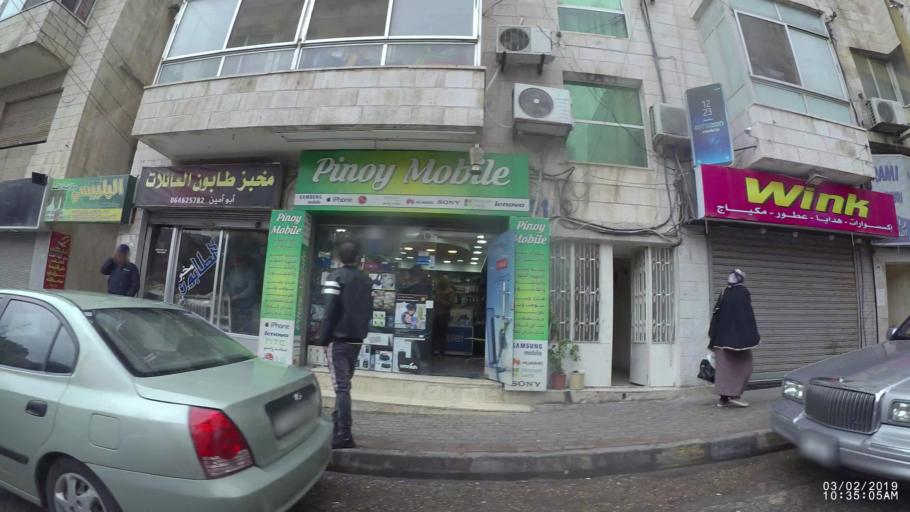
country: JO
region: Amman
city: Amman
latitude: 31.9486
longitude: 35.9187
